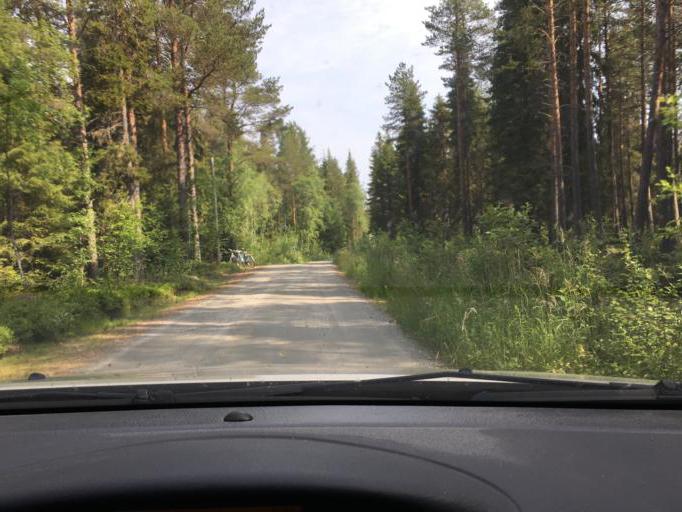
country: SE
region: Norrbotten
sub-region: Kalix Kommun
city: Rolfs
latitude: 65.7634
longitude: 22.9970
